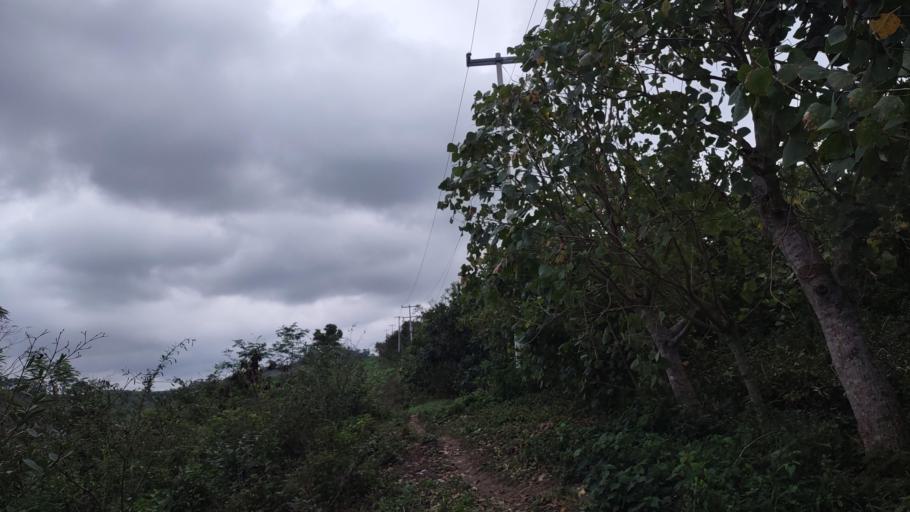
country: MX
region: Veracruz
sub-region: Coatzintla
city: Manuel Maria Contreras
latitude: 20.4133
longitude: -97.4576
